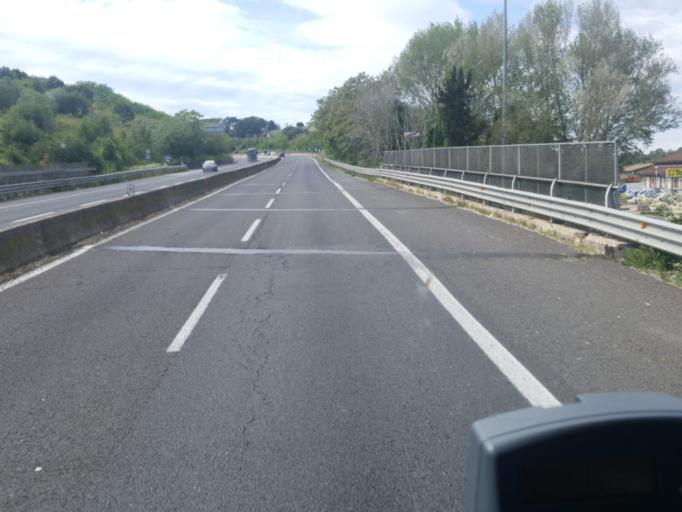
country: IT
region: Latium
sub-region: Citta metropolitana di Roma Capitale
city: Ara Nova
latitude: 41.9080
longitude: 12.2626
